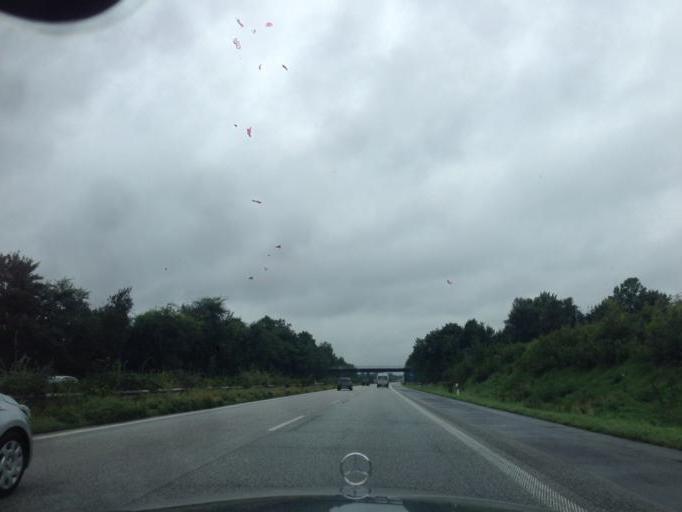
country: DE
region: Schleswig-Holstein
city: Schulldorf
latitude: 54.2826
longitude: 9.7706
